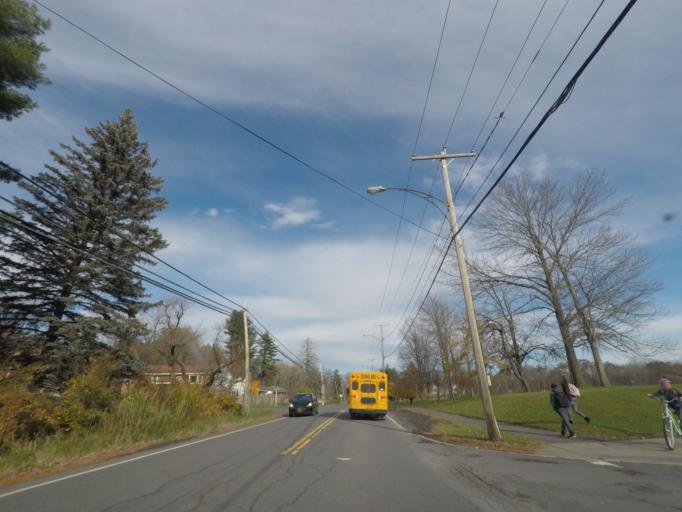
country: US
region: New York
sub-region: Albany County
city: Delmar
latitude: 42.6139
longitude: -73.8560
